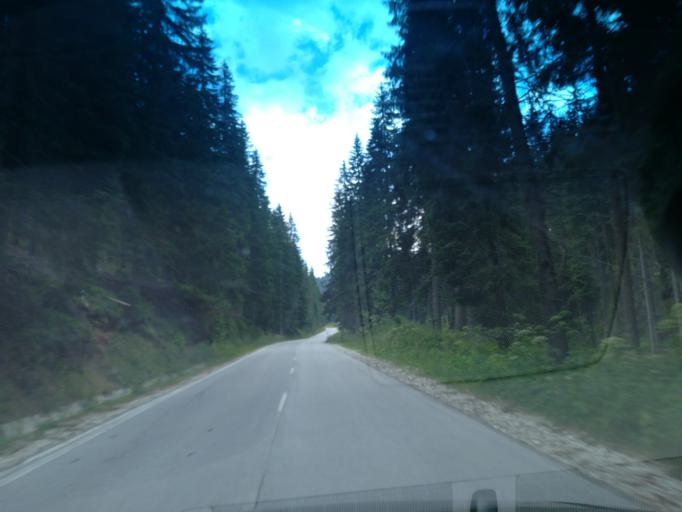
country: BG
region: Smolyan
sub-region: Obshtina Chepelare
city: Chepelare
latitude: 41.6602
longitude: 24.6814
